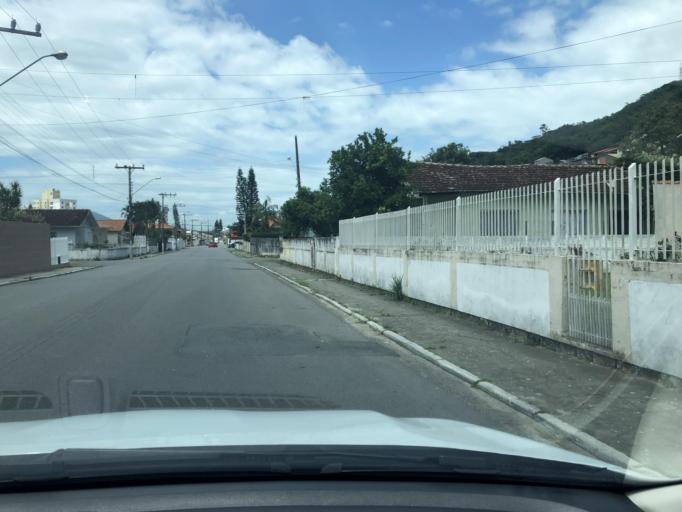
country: BR
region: Santa Catarina
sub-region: Florianopolis
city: Saco dos Limoes
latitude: -27.6047
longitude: -48.5367
